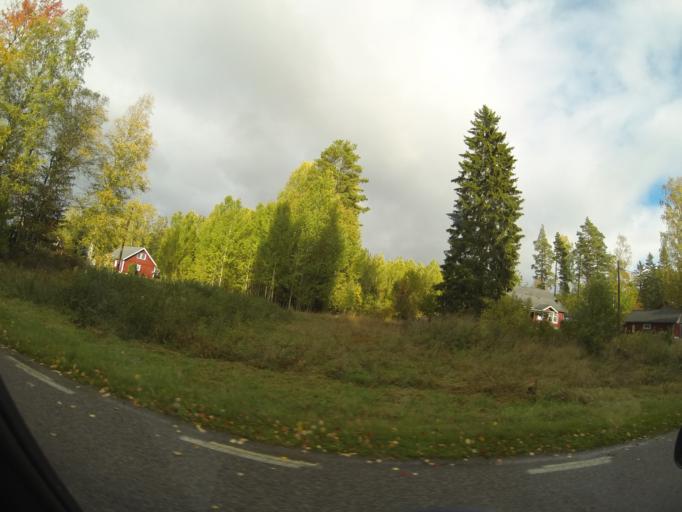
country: SE
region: Soedermanland
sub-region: Eskilstuna Kommun
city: Kvicksund
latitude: 59.3283
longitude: 16.2580
